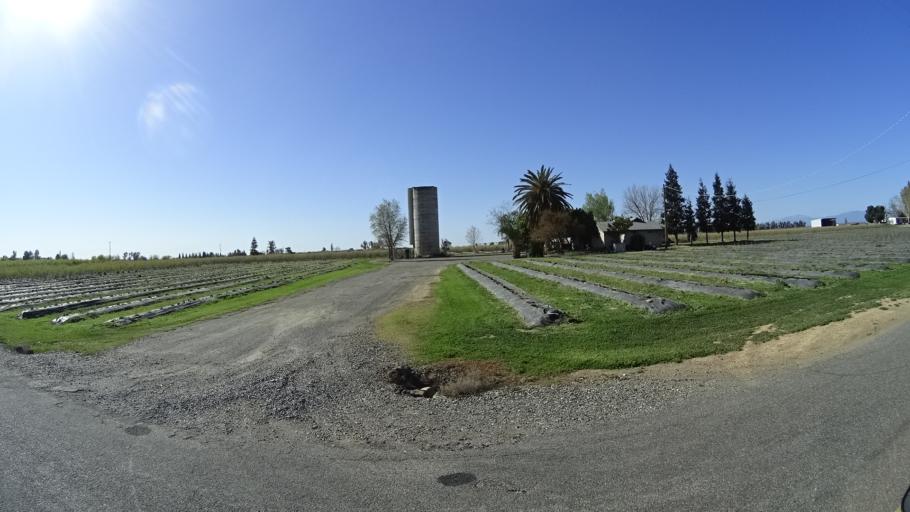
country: US
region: California
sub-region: Glenn County
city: Orland
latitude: 39.7442
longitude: -122.2322
